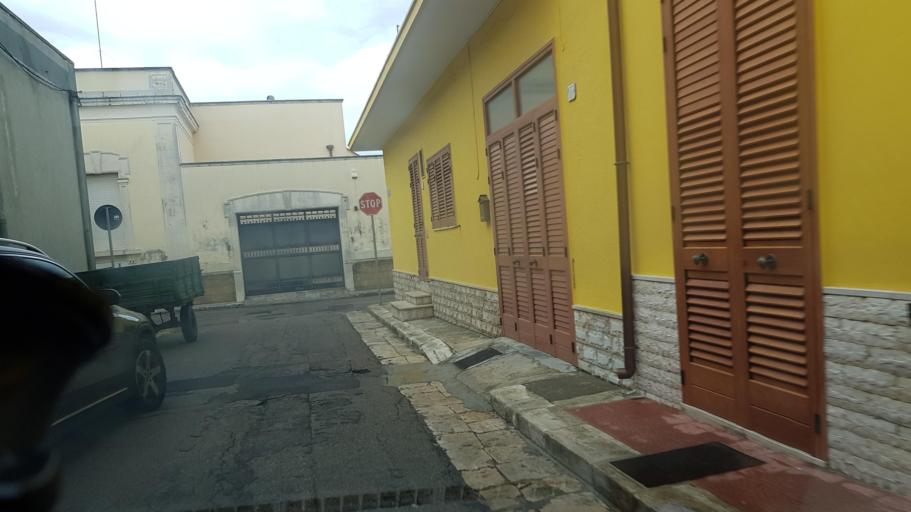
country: IT
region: Apulia
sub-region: Provincia di Lecce
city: Guagnano
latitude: 40.4003
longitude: 17.9523
